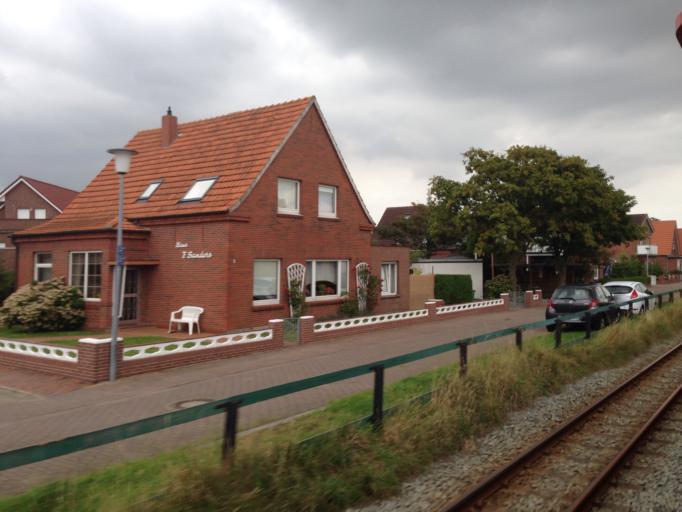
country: DE
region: Lower Saxony
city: Borkum
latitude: 53.5818
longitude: 6.6704
